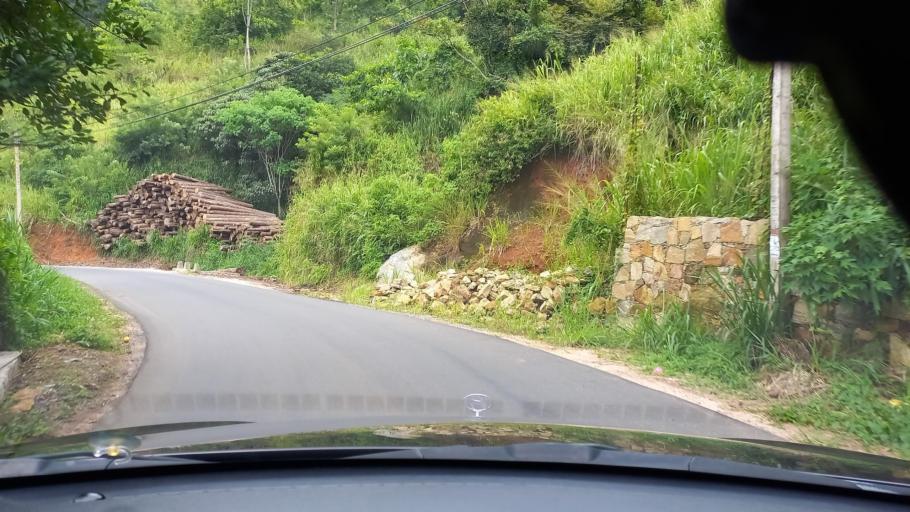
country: LK
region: Central
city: Gampola
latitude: 7.2044
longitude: 80.6310
